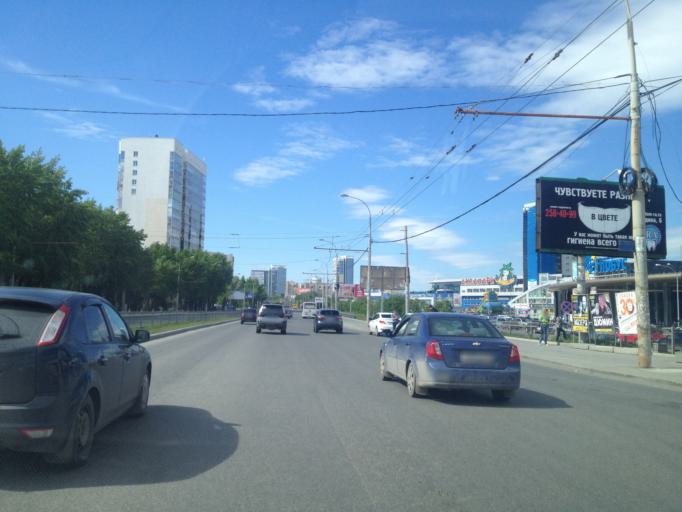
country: RU
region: Sverdlovsk
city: Yekaterinburg
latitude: 56.7875
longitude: 60.6478
